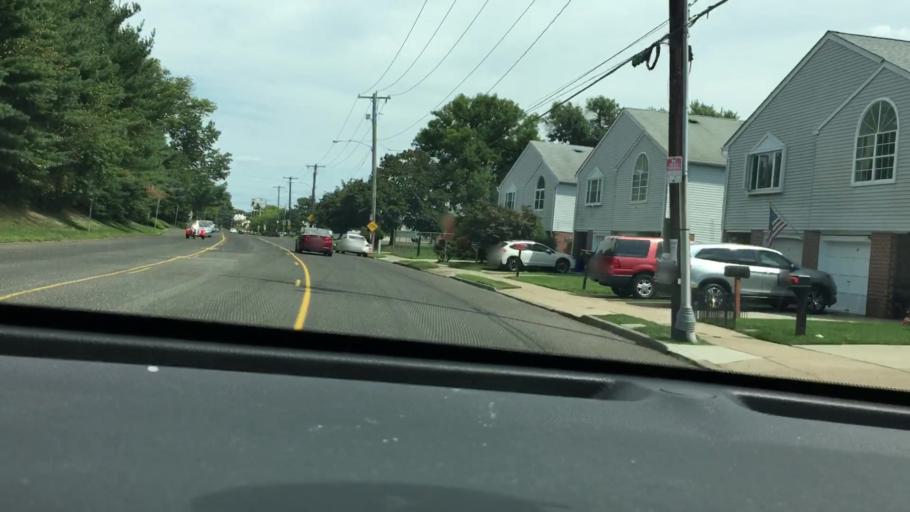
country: US
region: Pennsylvania
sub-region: Bucks County
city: Feasterville
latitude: 40.1294
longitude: -75.0205
